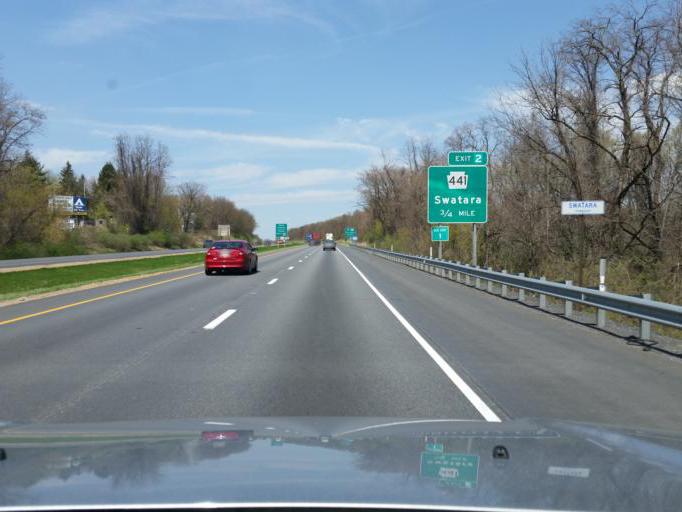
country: US
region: Pennsylvania
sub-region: Dauphin County
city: Highspire
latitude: 40.2309
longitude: -76.7953
